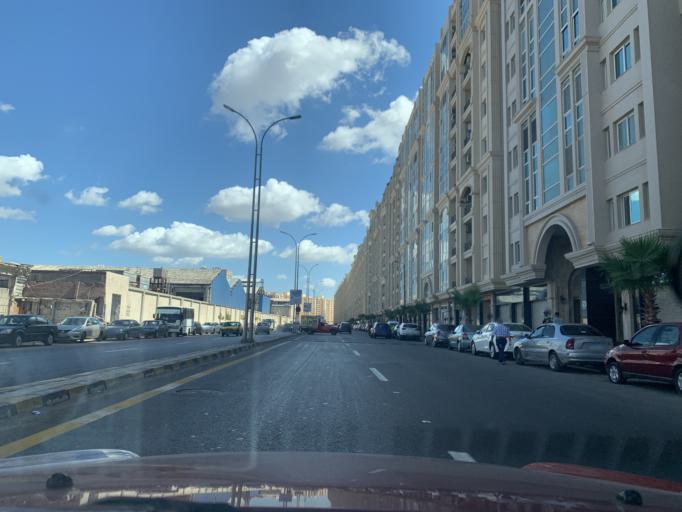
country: EG
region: Alexandria
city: Alexandria
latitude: 31.2186
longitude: 29.9498
